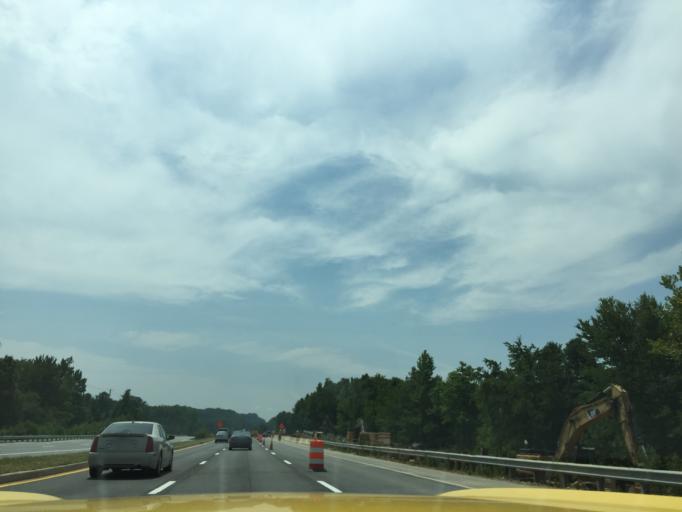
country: US
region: Maryland
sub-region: Prince George's County
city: Friendly
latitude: 38.7343
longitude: -76.9910
